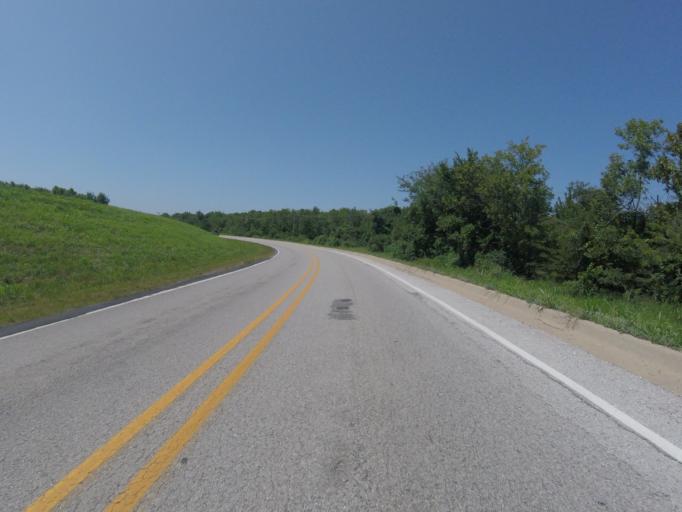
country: US
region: Arkansas
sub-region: Washington County
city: Johnson
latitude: 36.1065
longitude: -94.1823
